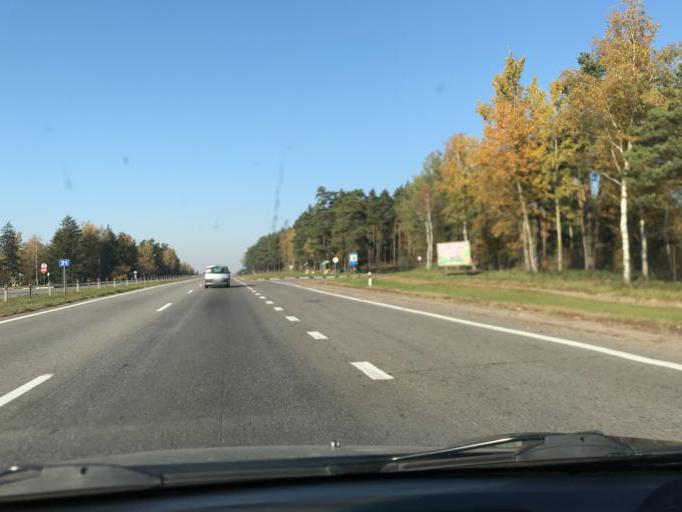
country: BY
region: Minsk
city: Dukora
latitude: 53.7107
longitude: 27.8731
